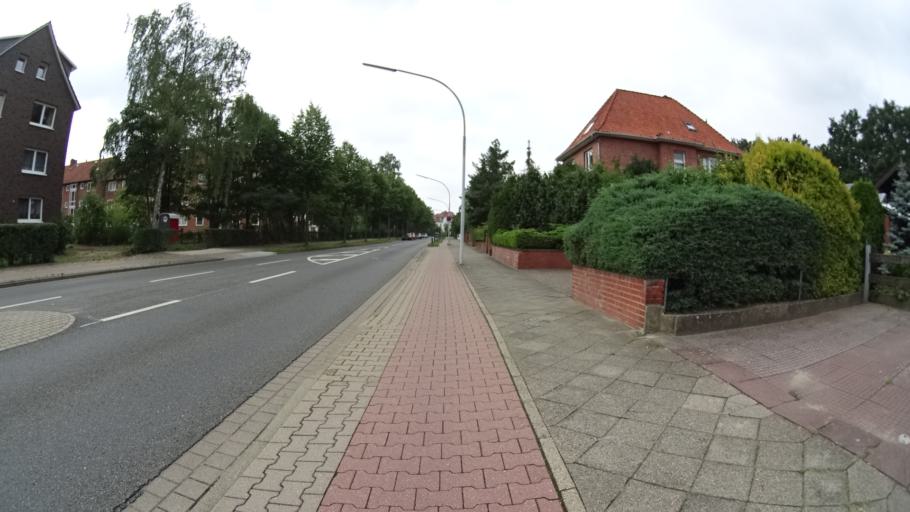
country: DE
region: Lower Saxony
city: Lueneburg
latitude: 53.2317
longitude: 10.3999
